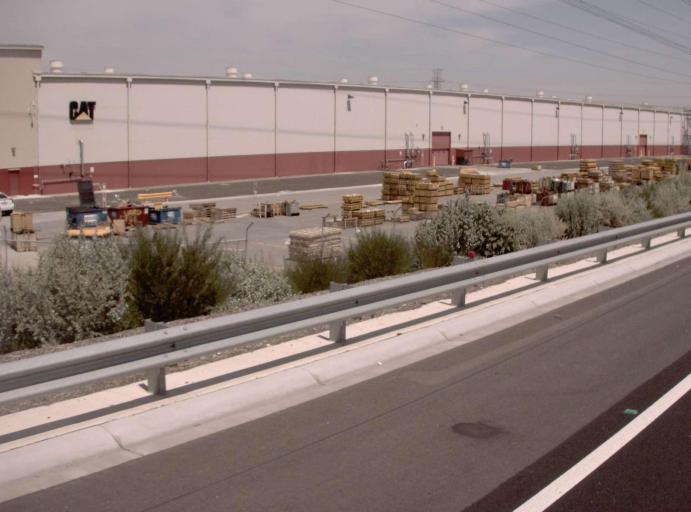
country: AU
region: Victoria
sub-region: Hume
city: Tullamarine
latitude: -37.7124
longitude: 144.8800
